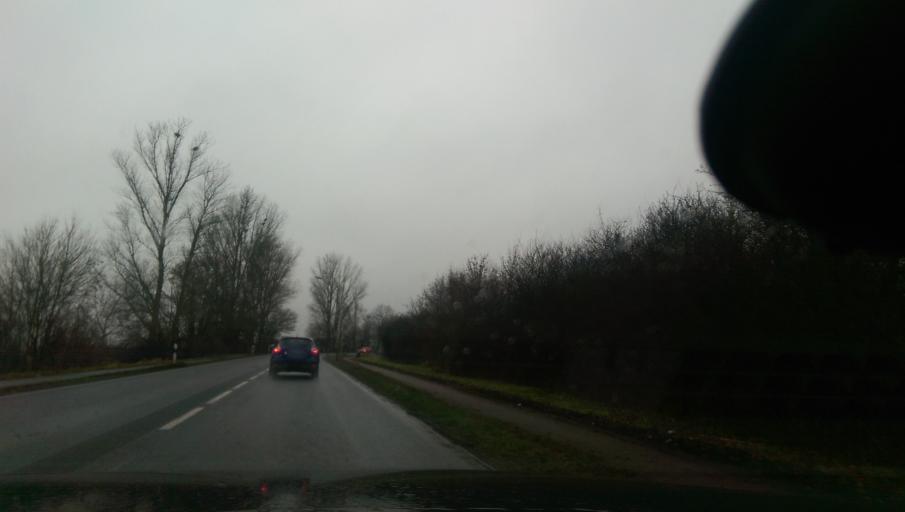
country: DE
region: Lower Saxony
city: Verden
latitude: 52.9221
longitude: 9.2195
